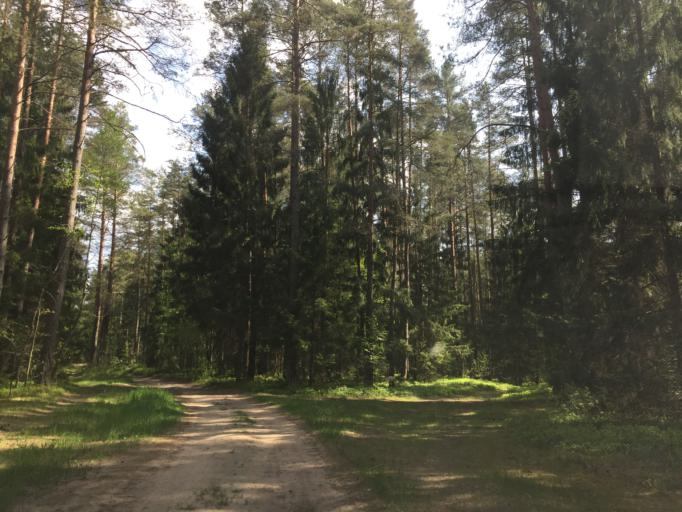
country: LV
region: Baldone
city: Baldone
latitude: 56.8009
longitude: 24.4287
